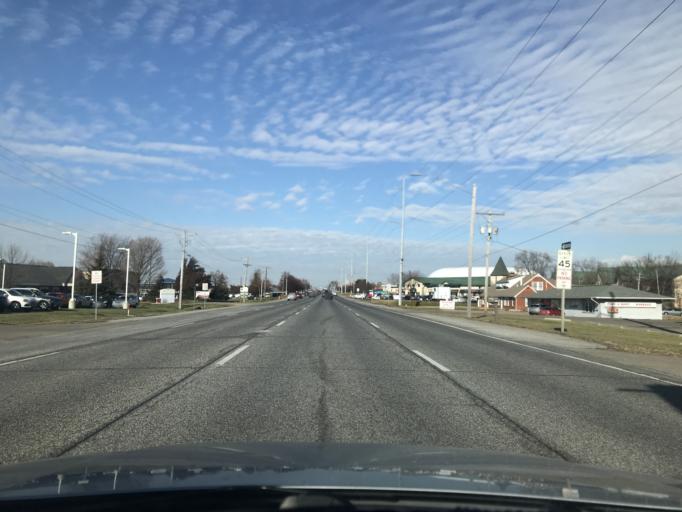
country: US
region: Iowa
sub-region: Scott County
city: Davenport
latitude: 41.5678
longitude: -90.5680
